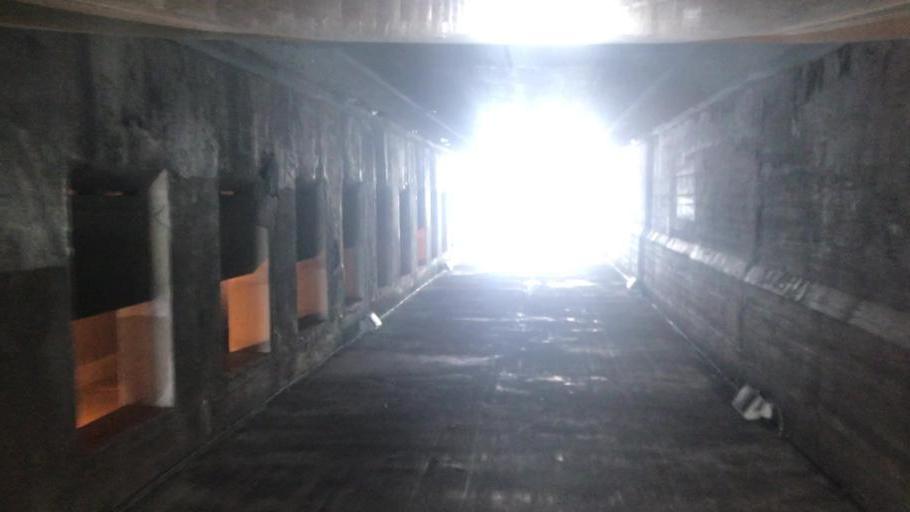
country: US
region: Texas
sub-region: Harris County
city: Houston
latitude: 29.7715
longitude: -95.3594
